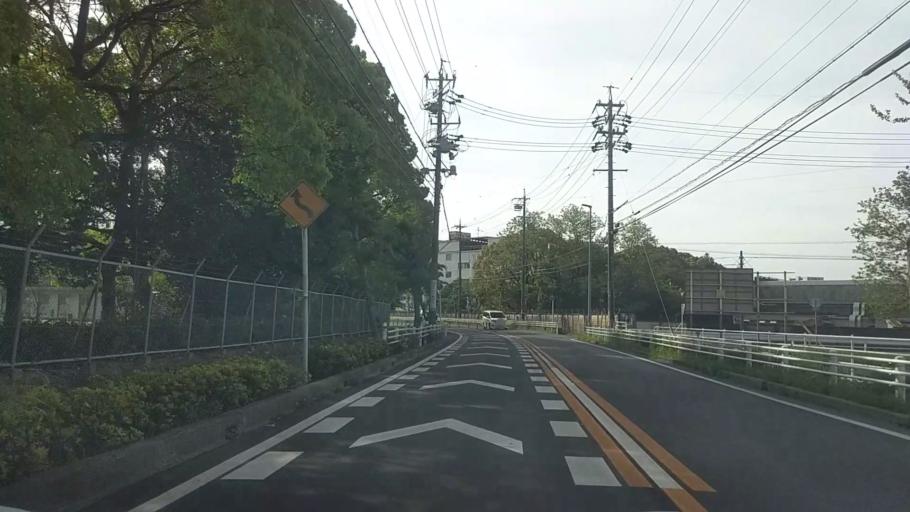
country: JP
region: Aichi
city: Anjo
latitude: 34.9684
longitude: 137.0766
